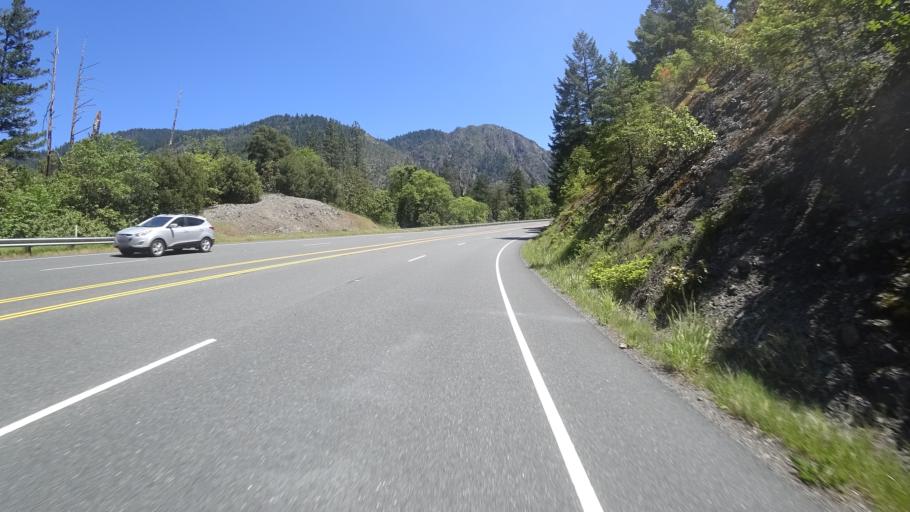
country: US
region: California
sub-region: Humboldt County
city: Willow Creek
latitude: 40.8625
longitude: -123.5022
